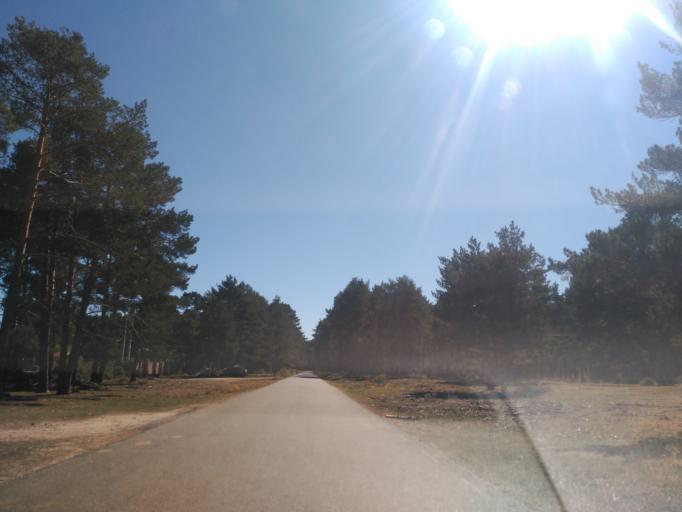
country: ES
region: Castille and Leon
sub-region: Provincia de Soria
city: Vinuesa
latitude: 41.9368
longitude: -2.7785
